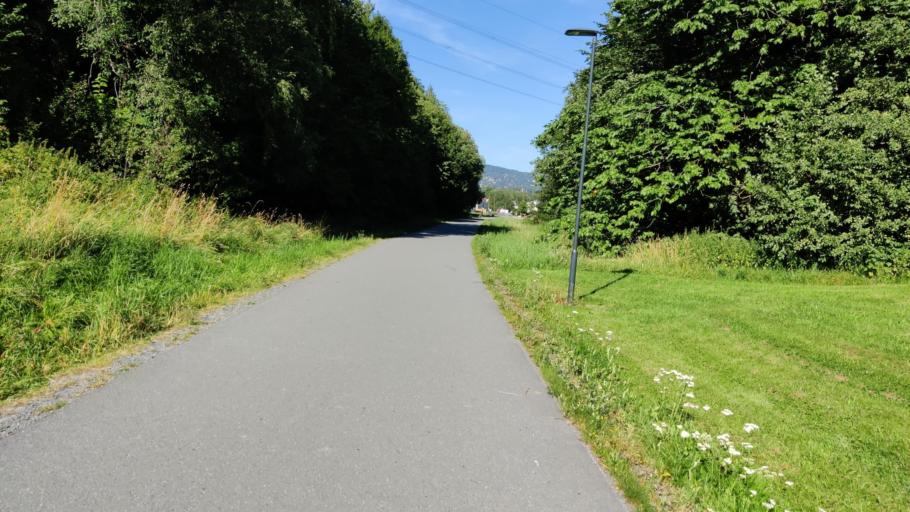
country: NO
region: Akershus
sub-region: Baerum
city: Lysaker
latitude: 59.9329
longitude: 10.6068
